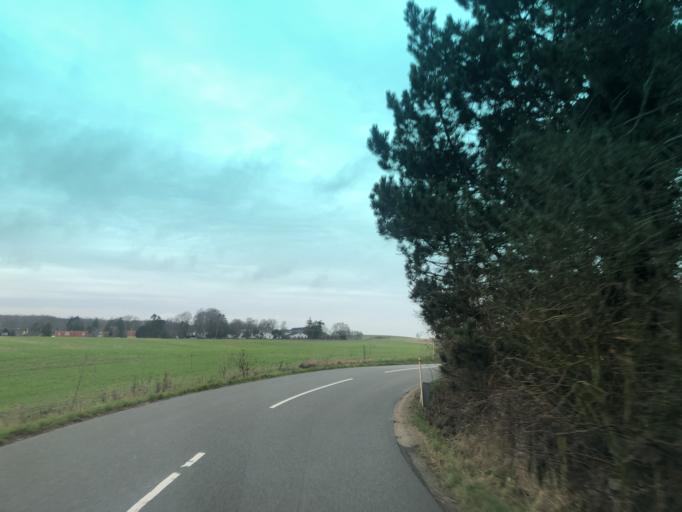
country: DK
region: Capital Region
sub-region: Frederikssund Kommune
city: Slangerup
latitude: 55.8602
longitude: 12.2296
